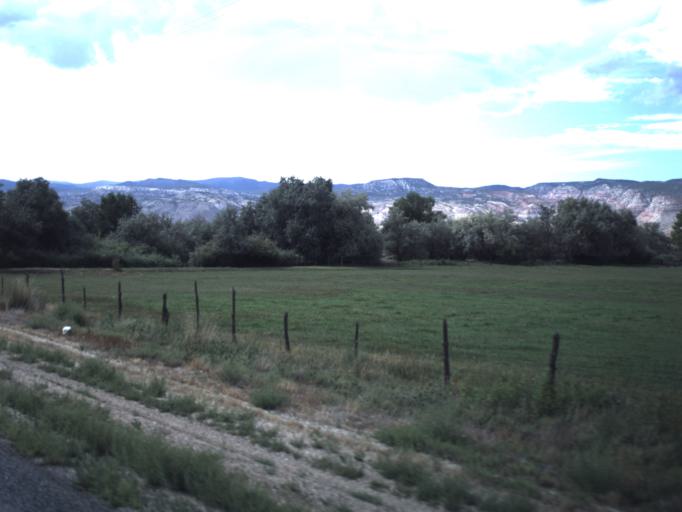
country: US
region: Utah
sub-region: Sevier County
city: Richfield
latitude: 38.7741
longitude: -112.0280
